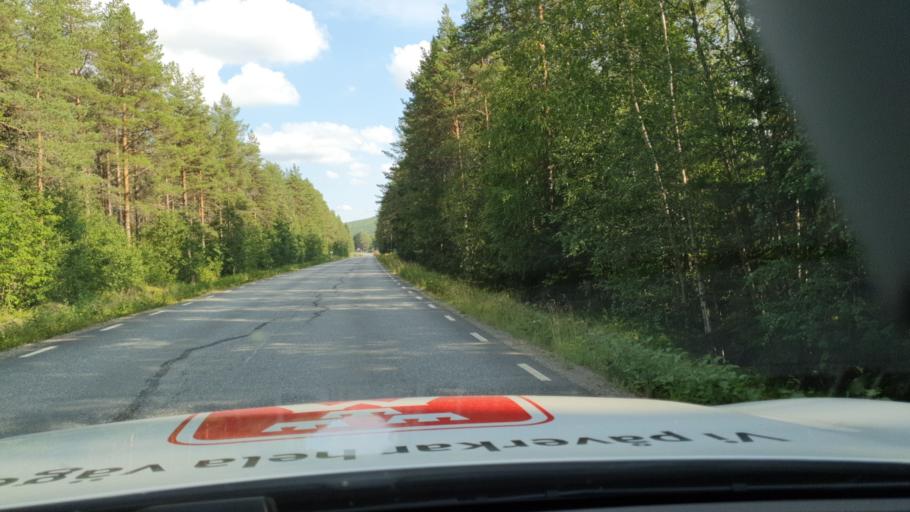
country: SE
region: Vaesterbotten
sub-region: Dorotea Kommun
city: Dorotea
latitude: 64.2630
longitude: 16.3650
